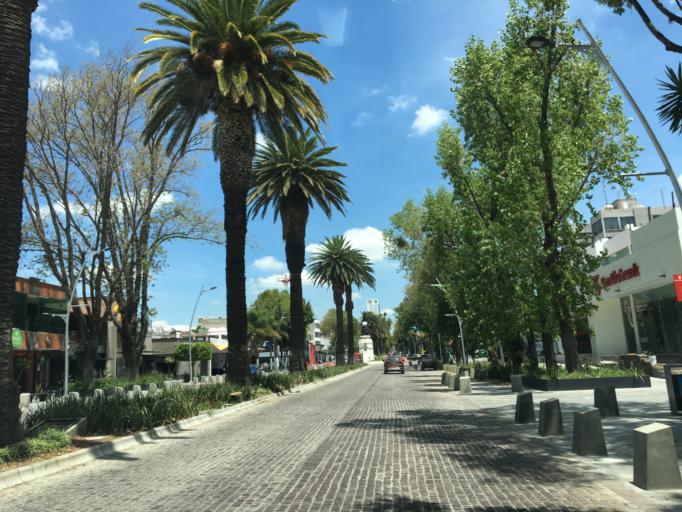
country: MX
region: Puebla
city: Puebla
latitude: 19.0485
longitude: -98.2121
